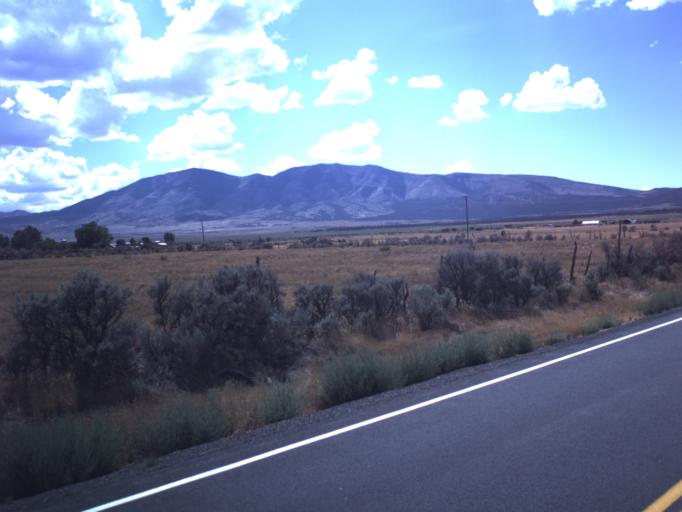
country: US
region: Utah
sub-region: Tooele County
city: Tooele
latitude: 40.3368
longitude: -112.4354
